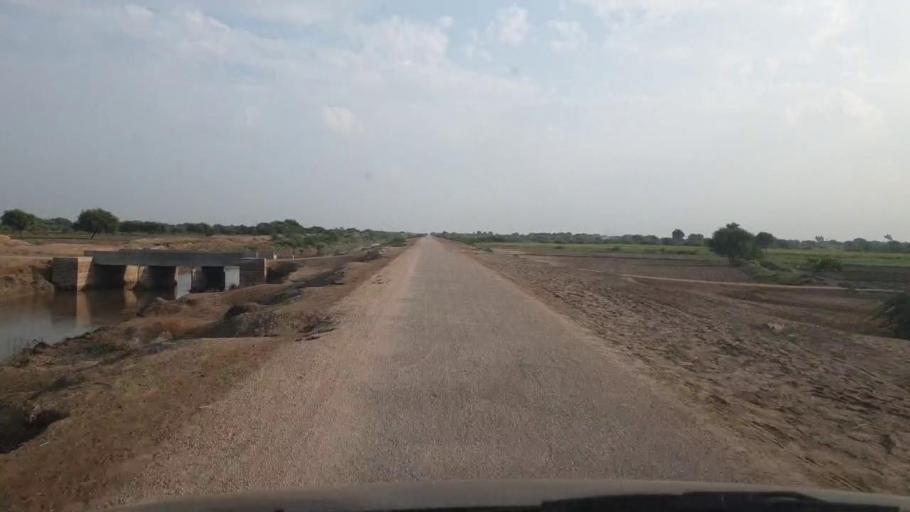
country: PK
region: Sindh
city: Badin
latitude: 24.5395
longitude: 68.6747
